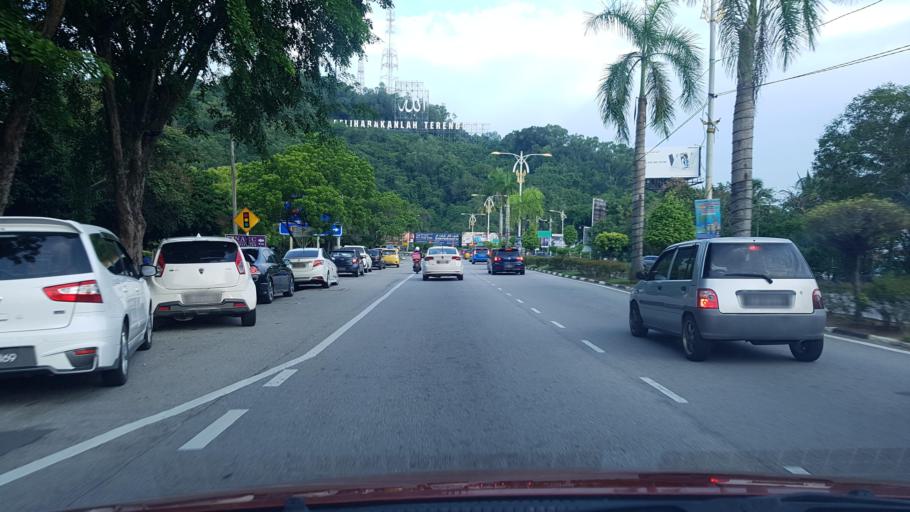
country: MY
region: Terengganu
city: Kuala Terengganu
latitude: 5.3122
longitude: 103.1313
